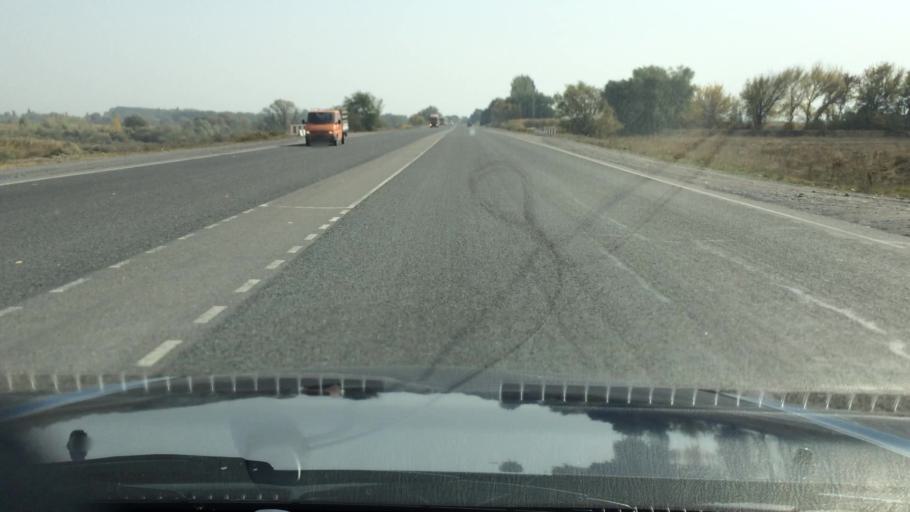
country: KG
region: Chuy
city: Kant
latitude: 42.9449
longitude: 74.9613
